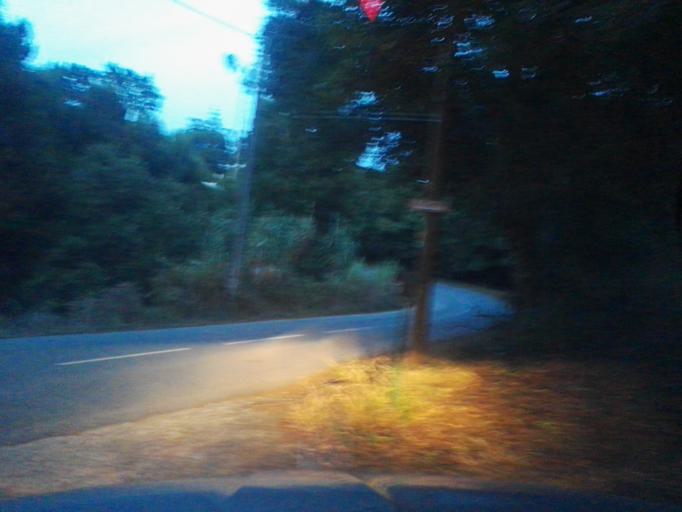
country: PT
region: Lisbon
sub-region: Sintra
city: Colares
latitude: 38.7896
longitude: -9.4592
